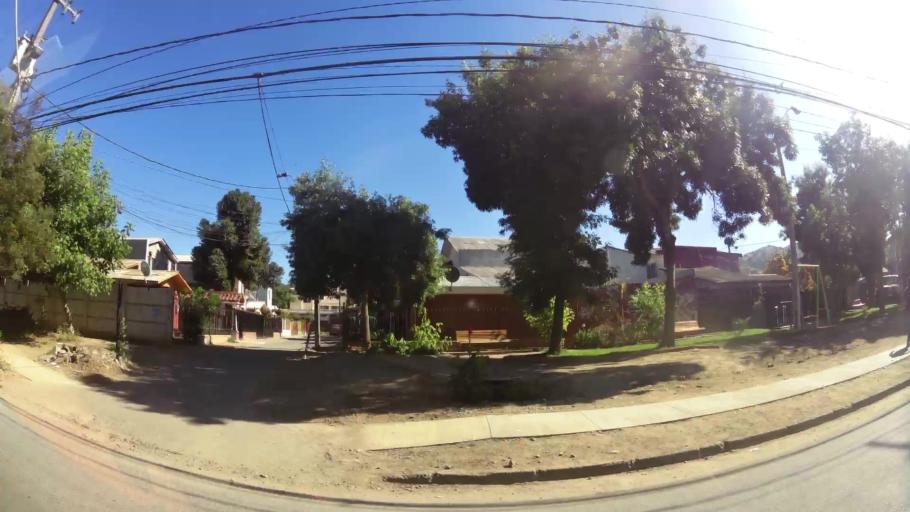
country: CL
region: Santiago Metropolitan
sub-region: Provincia de Chacabuco
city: Lampa
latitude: -33.4052
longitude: -71.1282
